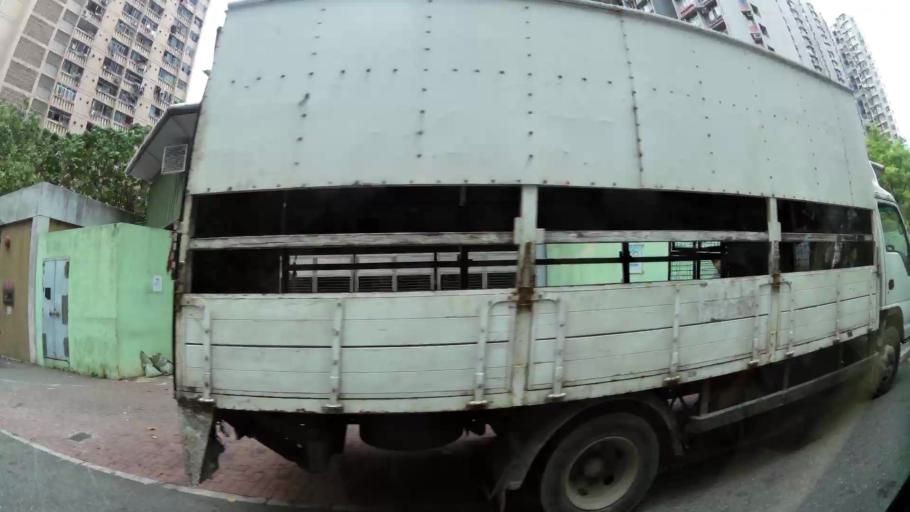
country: HK
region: Kowloon City
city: Kowloon
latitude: 22.3164
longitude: 114.2335
